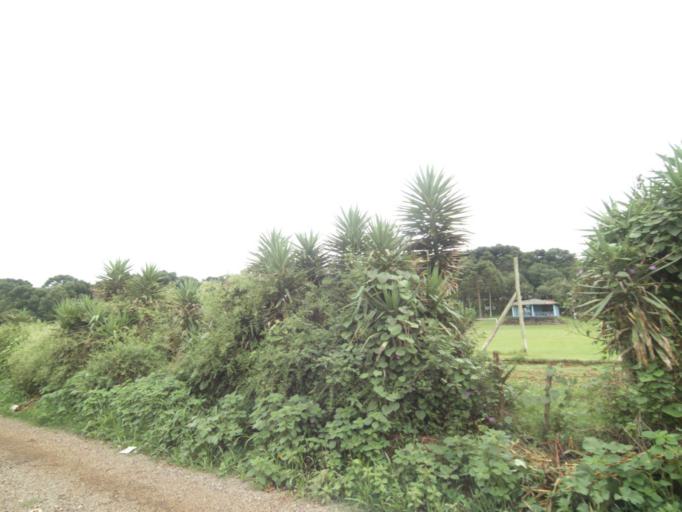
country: BR
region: Rio Grande do Sul
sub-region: Lagoa Vermelha
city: Lagoa Vermelha
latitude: -28.2224
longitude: -51.5245
